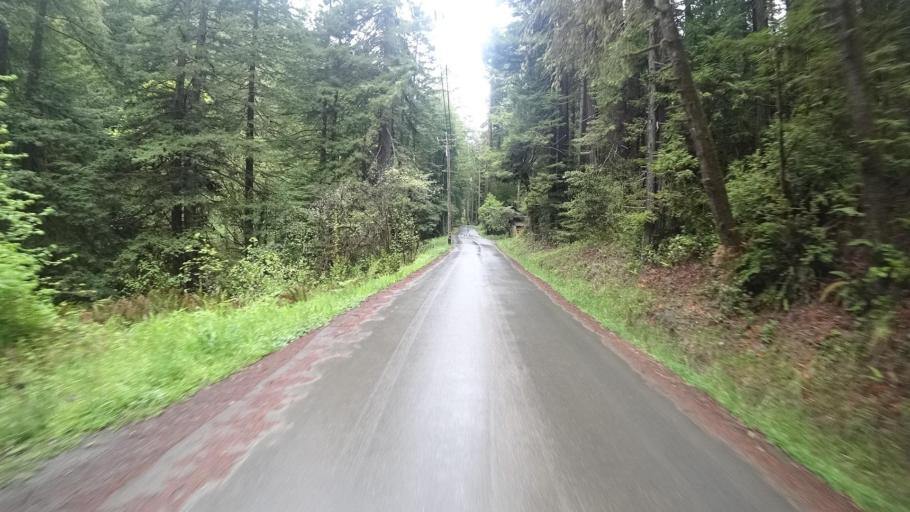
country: US
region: California
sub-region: Humboldt County
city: Bayside
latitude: 40.8119
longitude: -124.0244
